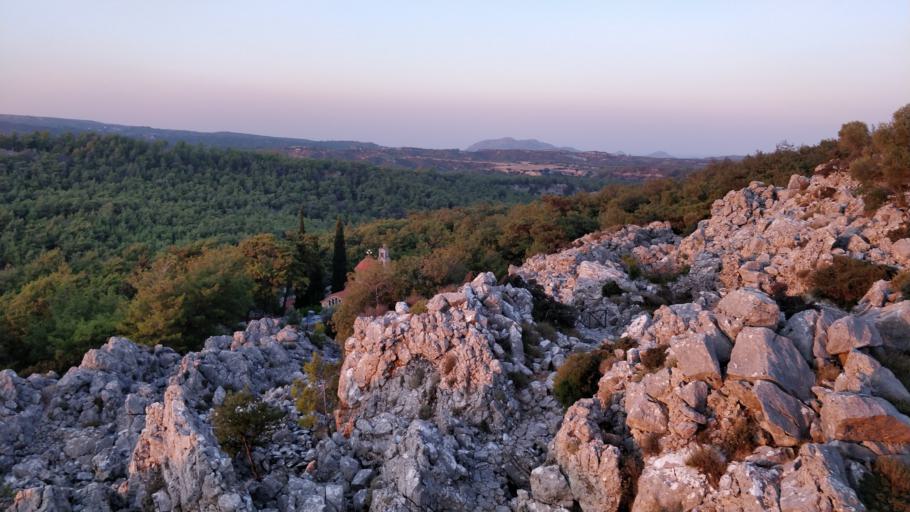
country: GR
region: South Aegean
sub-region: Nomos Dodekanisou
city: Archangelos
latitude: 36.2638
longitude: 28.0758
